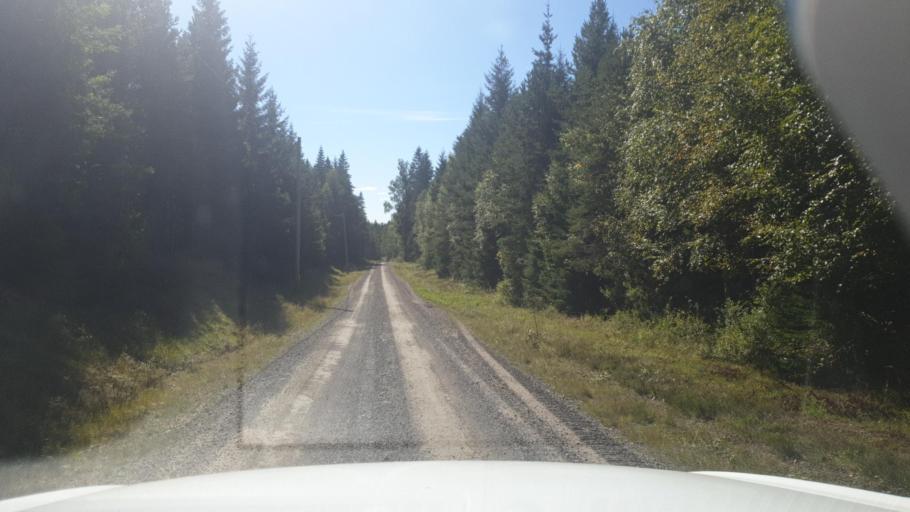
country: SE
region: Vaermland
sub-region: Eda Kommun
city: Charlottenberg
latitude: 60.1561
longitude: 12.5997
